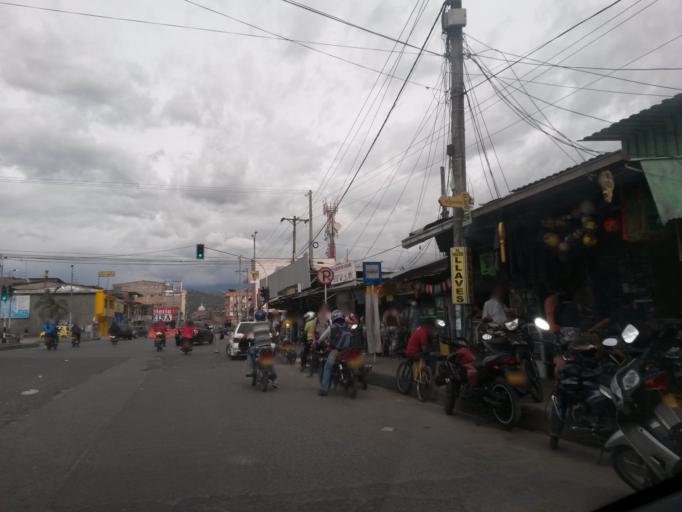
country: CO
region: Cauca
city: Popayan
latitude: 2.4450
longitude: -76.6152
